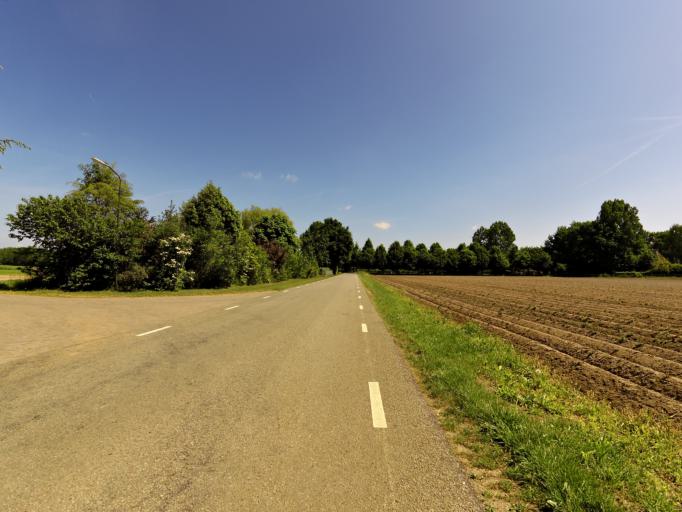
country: NL
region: Gelderland
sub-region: Gemeente Bronckhorst
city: Hengelo
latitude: 52.0625
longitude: 6.2813
